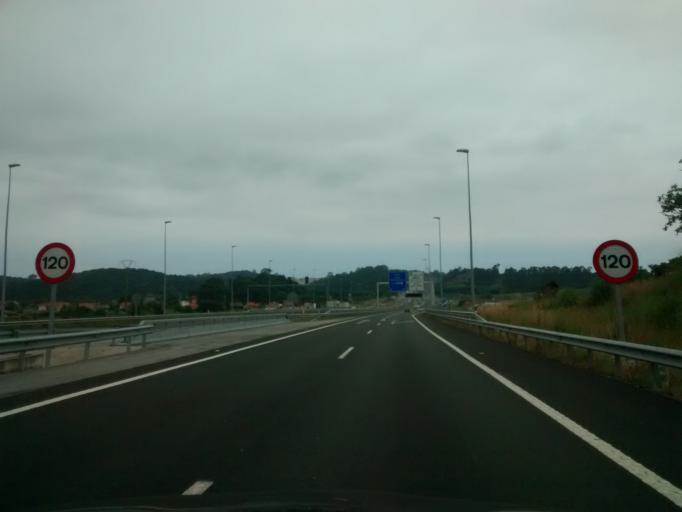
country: ES
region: Cantabria
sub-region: Provincia de Cantabria
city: Camargo
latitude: 43.3988
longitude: -3.8680
